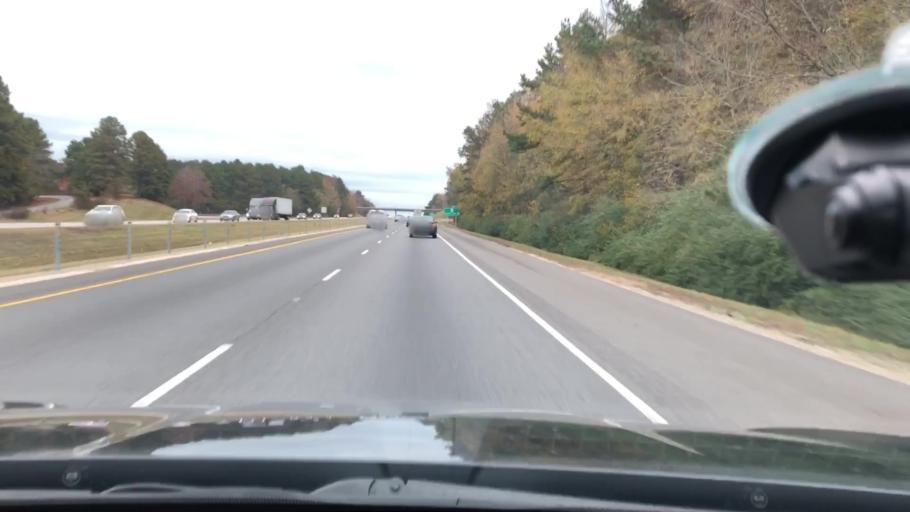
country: US
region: Arkansas
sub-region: Hot Spring County
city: Malvern
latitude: 34.3292
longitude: -92.9230
